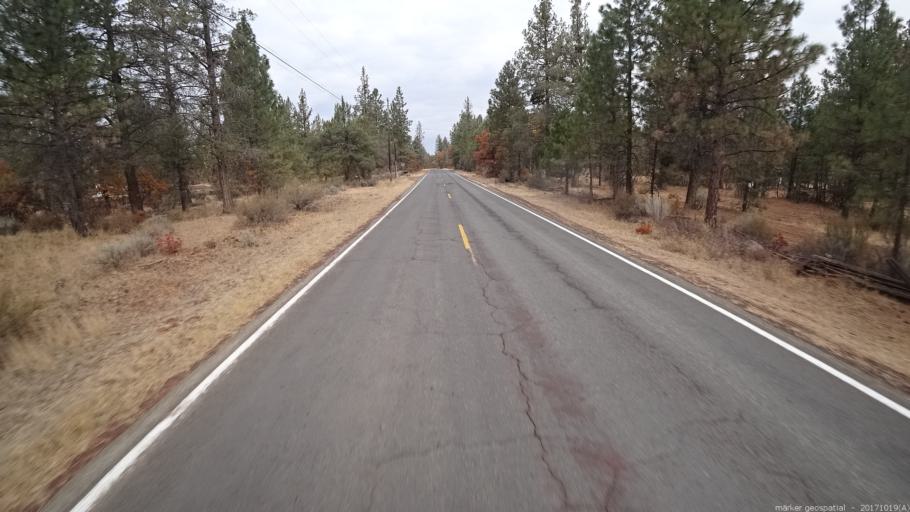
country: US
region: California
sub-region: Shasta County
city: Burney
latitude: 41.1099
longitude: -121.3294
